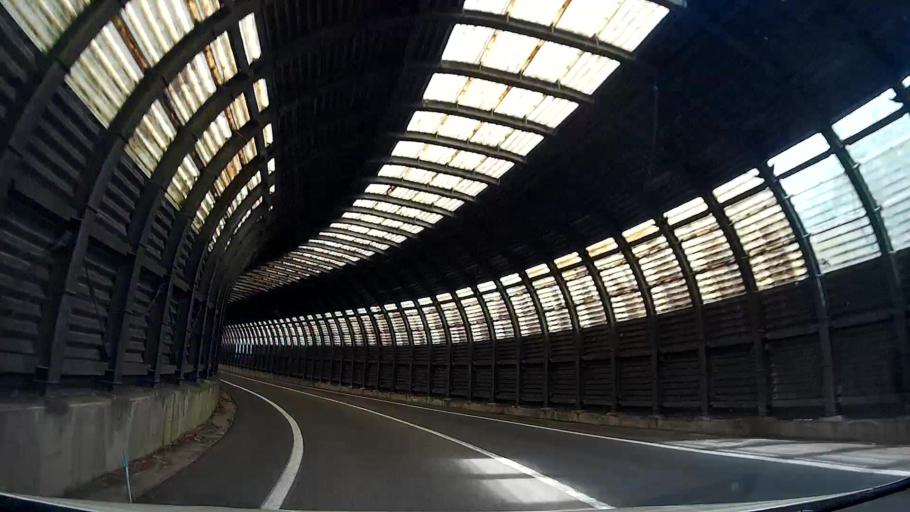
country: JP
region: Iwate
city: Shizukuishi
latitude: 39.9267
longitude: 140.9618
